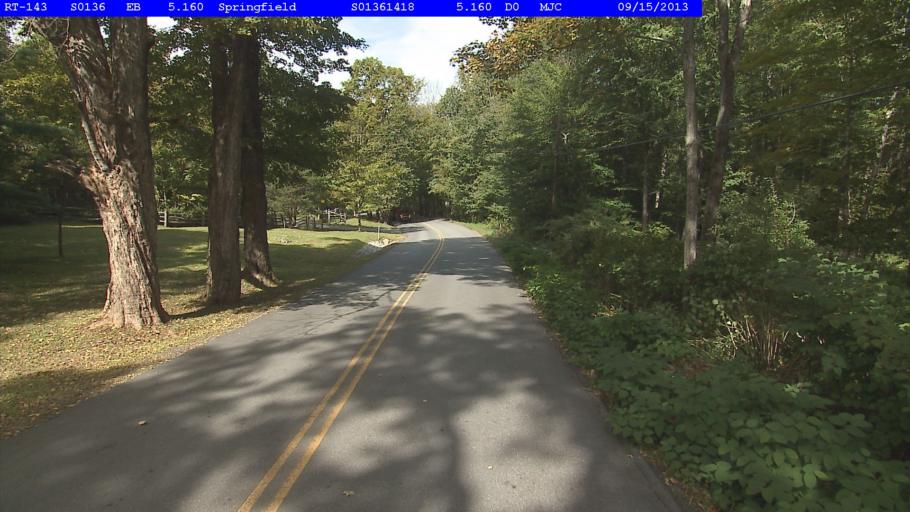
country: US
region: Vermont
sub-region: Windsor County
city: Springfield
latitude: 43.3230
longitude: -72.4124
